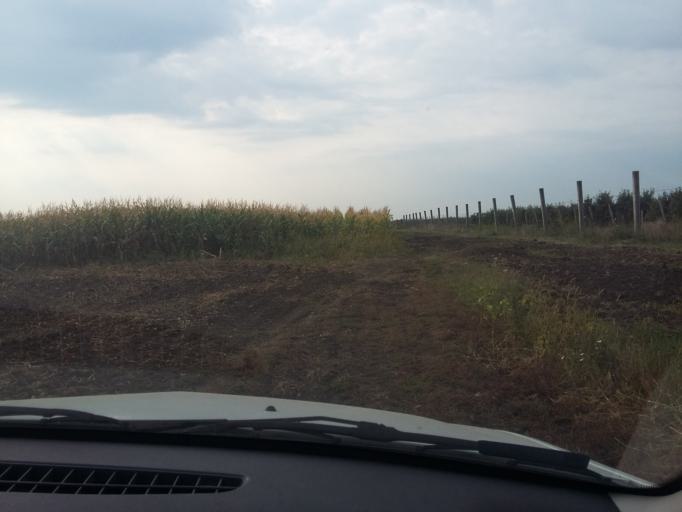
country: HU
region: Borsod-Abauj-Zemplen
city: Taktaharkany
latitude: 48.1292
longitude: 21.1071
